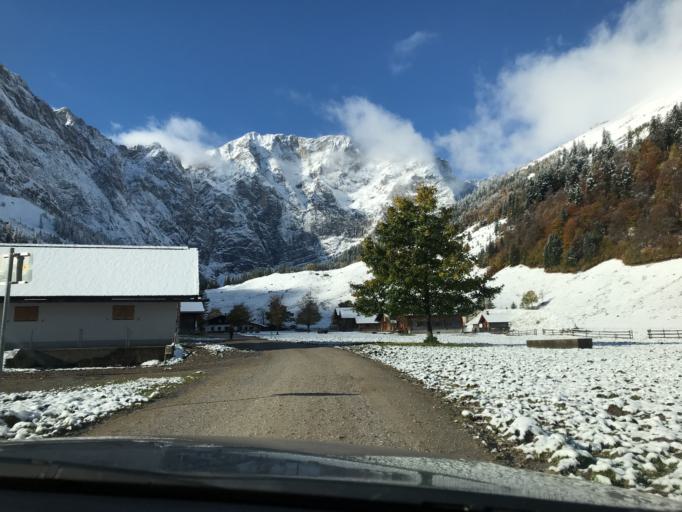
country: AT
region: Tyrol
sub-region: Politischer Bezirk Innsbruck Land
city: Gnadenwald
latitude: 47.4002
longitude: 11.5602
